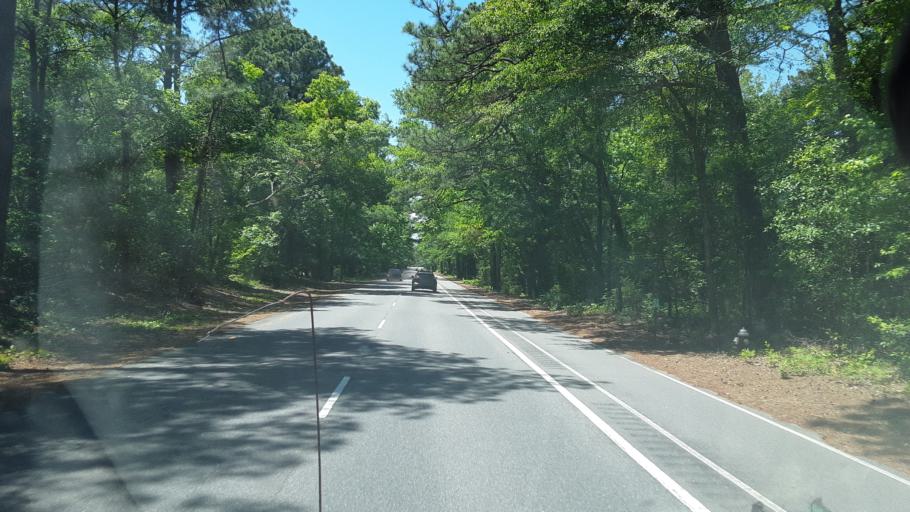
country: US
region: Virginia
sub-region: City of Virginia Beach
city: Virginia Beach
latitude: 36.9200
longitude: -76.0291
